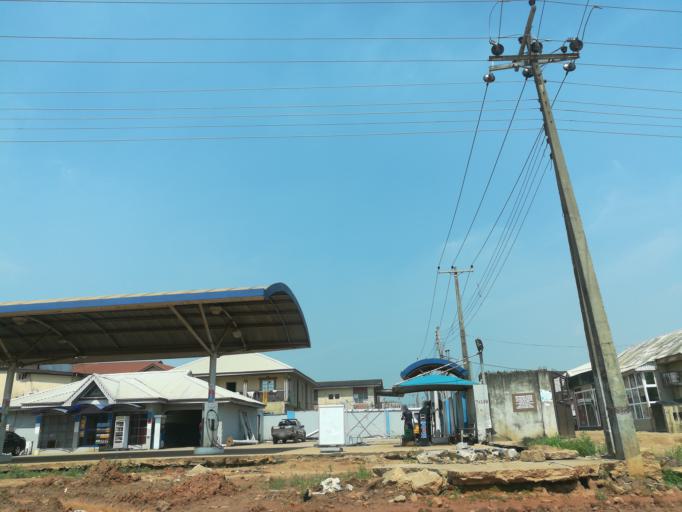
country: NG
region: Lagos
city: Ikorodu
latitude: 6.6519
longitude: 3.4760
